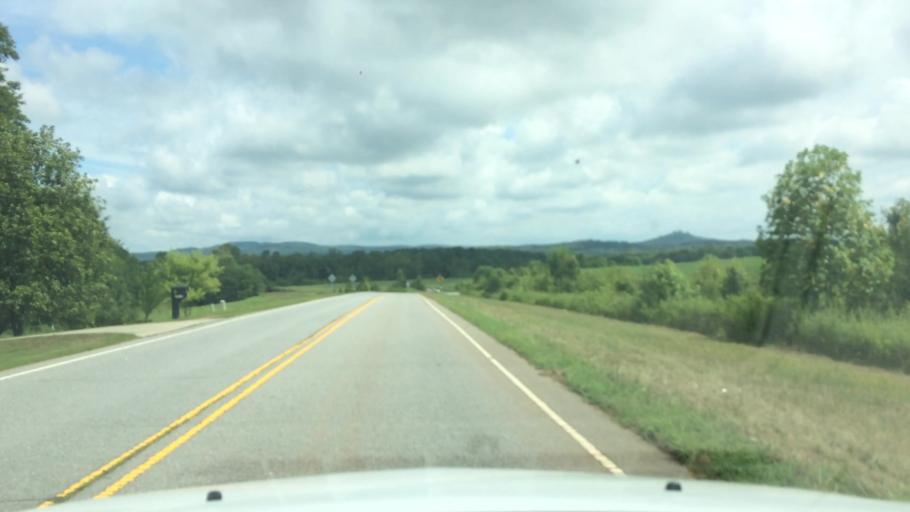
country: US
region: North Carolina
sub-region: Yadkin County
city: Jonesville
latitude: 36.1171
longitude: -80.8569
